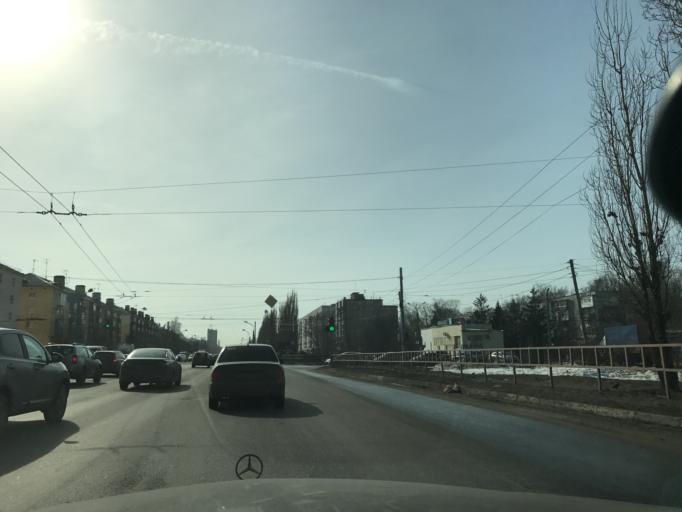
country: RU
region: Nizjnij Novgorod
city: Nizhniy Novgorod
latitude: 56.2848
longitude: 43.9275
